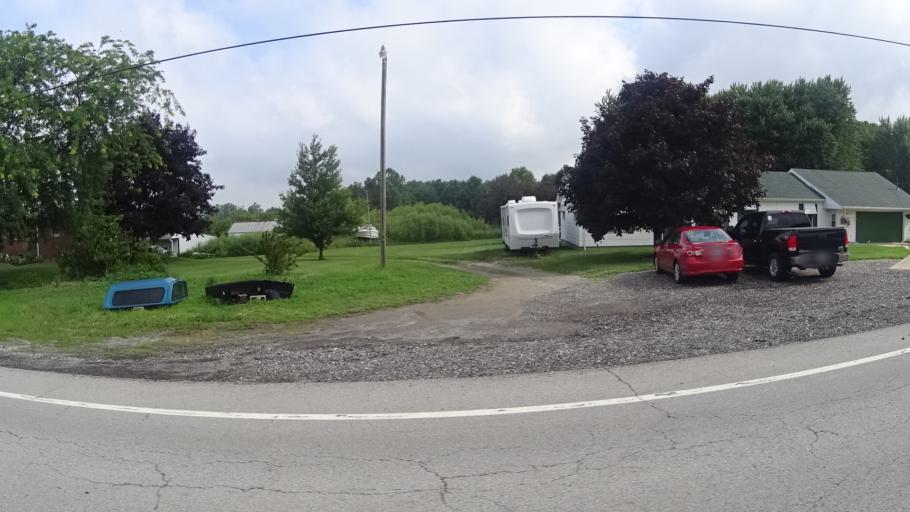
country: US
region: Ohio
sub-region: Huron County
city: Wakeman
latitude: 41.3051
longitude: -82.4876
